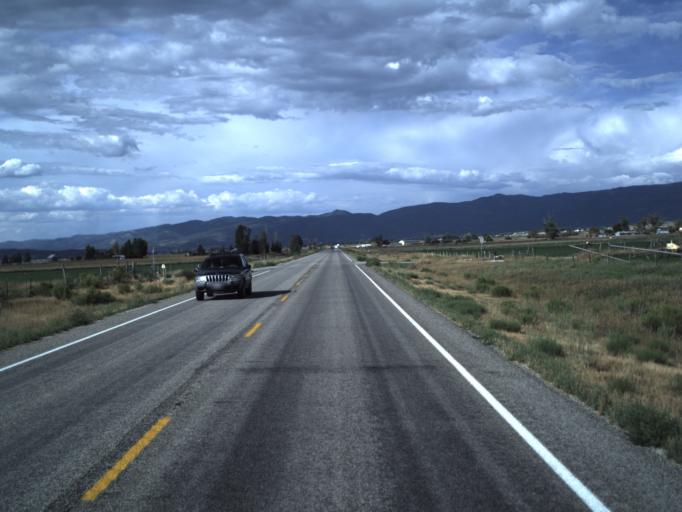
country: US
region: Utah
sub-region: Sanpete County
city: Mount Pleasant
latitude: 39.4965
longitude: -111.5082
